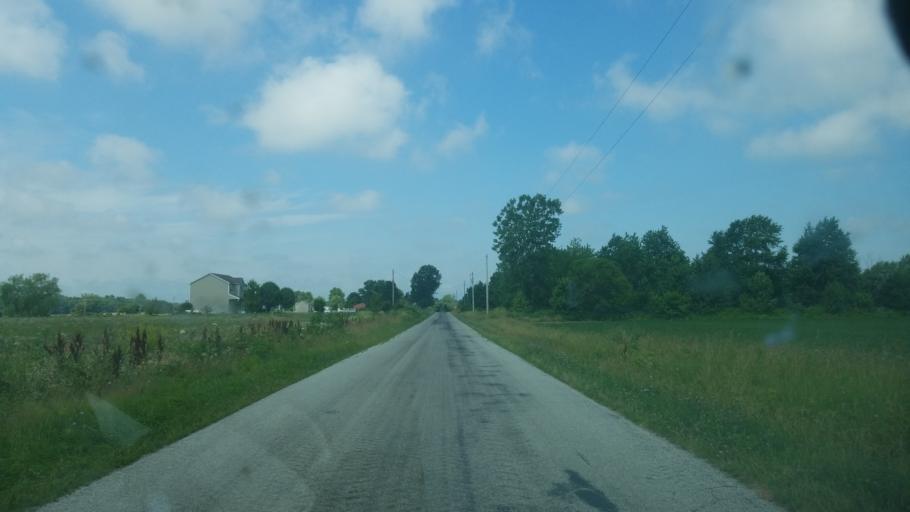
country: US
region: Ohio
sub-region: Licking County
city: Johnstown
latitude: 40.2079
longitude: -82.7510
